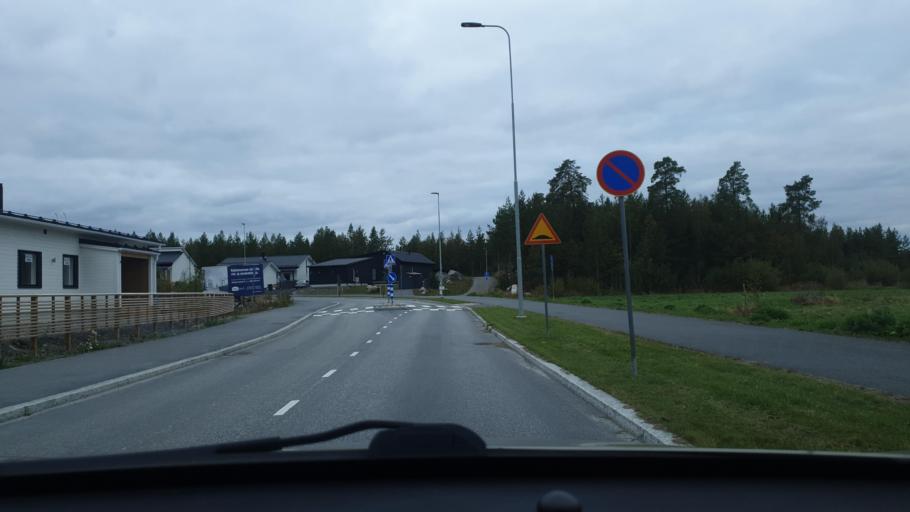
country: FI
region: Ostrobothnia
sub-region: Vaasa
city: Korsholm
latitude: 63.1292
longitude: 21.6581
